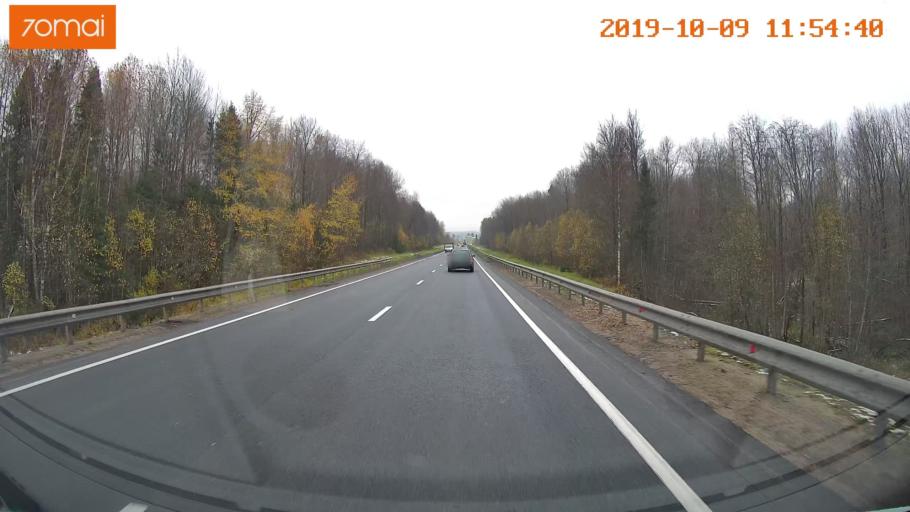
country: RU
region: Vologda
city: Gryazovets
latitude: 58.7564
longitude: 40.2825
